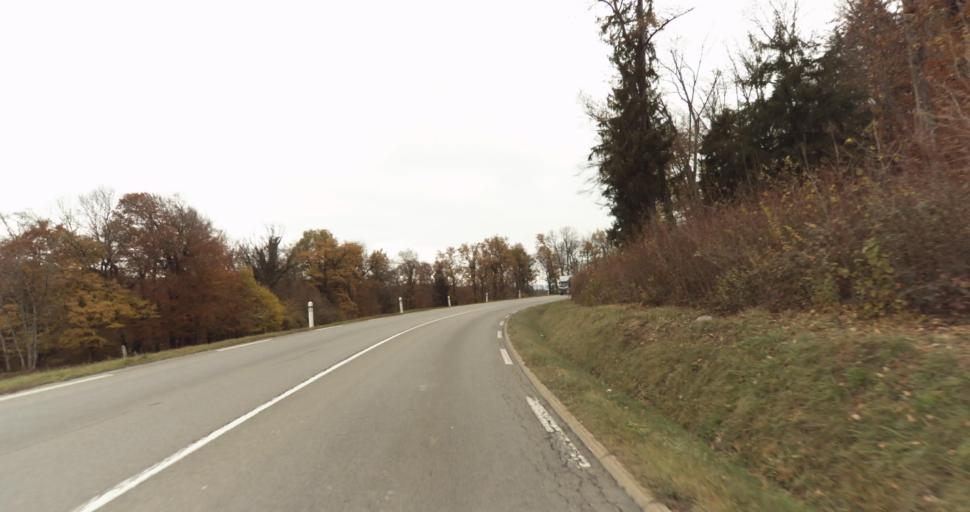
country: FR
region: Rhone-Alpes
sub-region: Departement de la Haute-Savoie
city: Pringy
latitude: 45.9579
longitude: 6.1257
